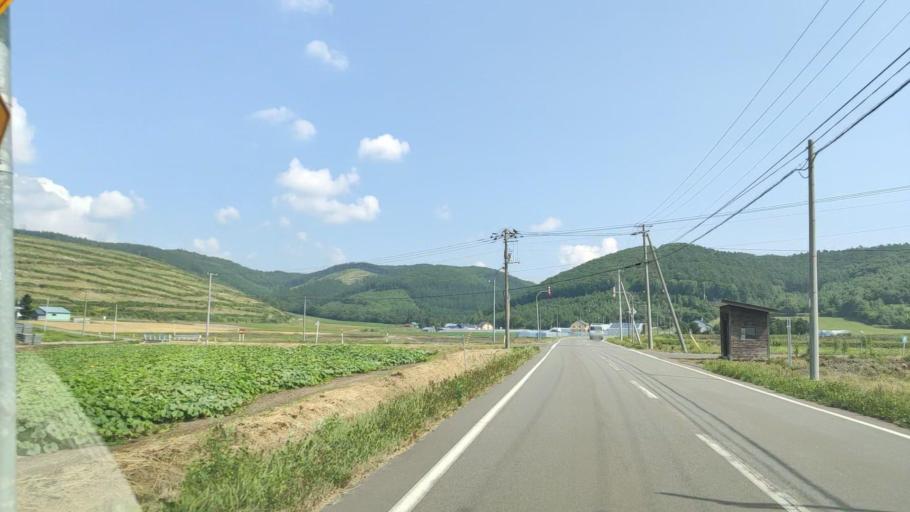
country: JP
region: Hokkaido
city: Shimo-furano
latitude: 43.4150
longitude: 142.3995
